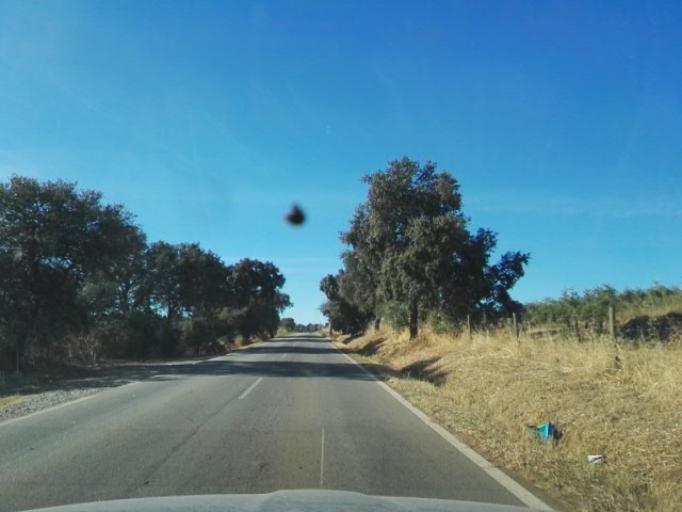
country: PT
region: Portalegre
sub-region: Elvas
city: Elvas
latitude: 38.9180
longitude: -7.1821
